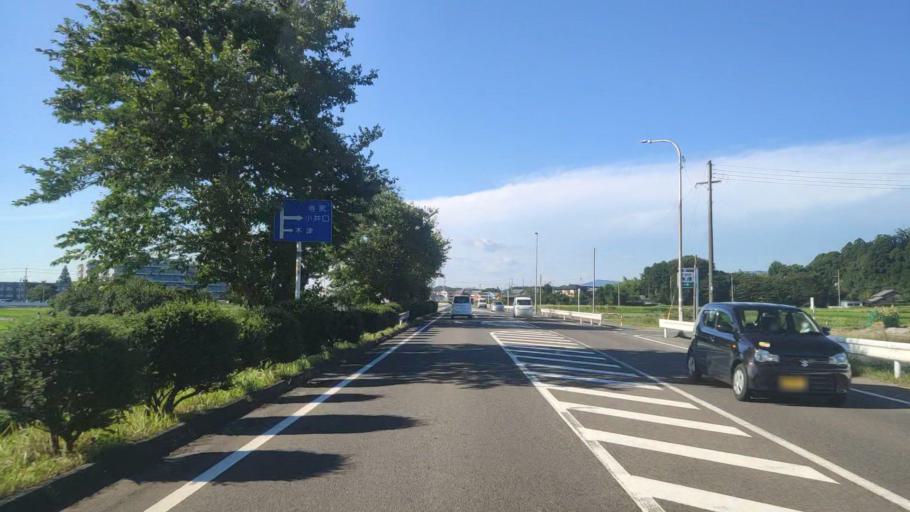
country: JP
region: Shiga Prefecture
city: Hino
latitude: 35.0085
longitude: 136.2398
